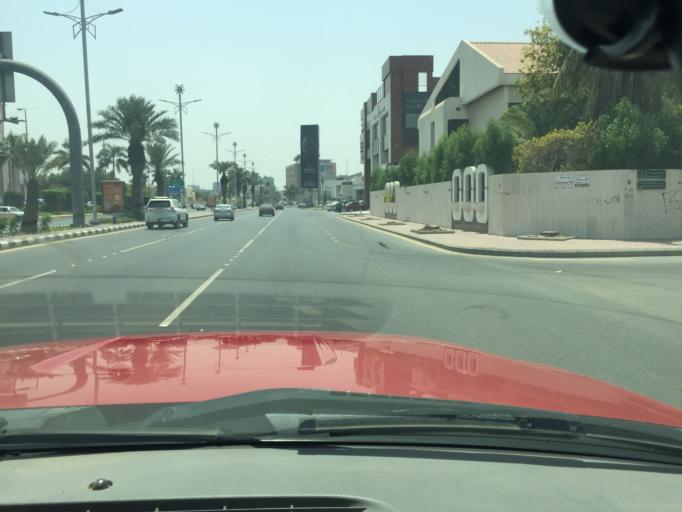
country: SA
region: Makkah
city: Jeddah
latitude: 21.5488
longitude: 39.1466
